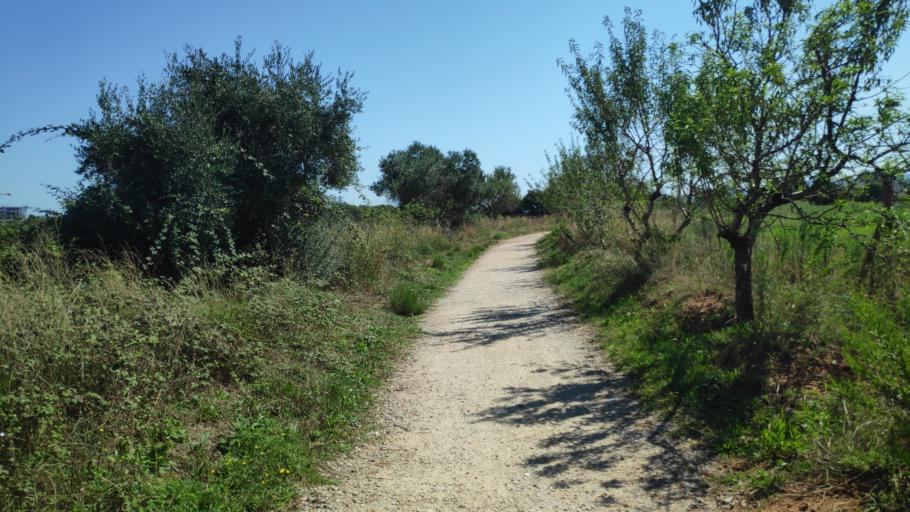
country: ES
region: Catalonia
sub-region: Provincia de Barcelona
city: Sant Quirze del Valles
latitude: 41.5457
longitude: 2.0741
